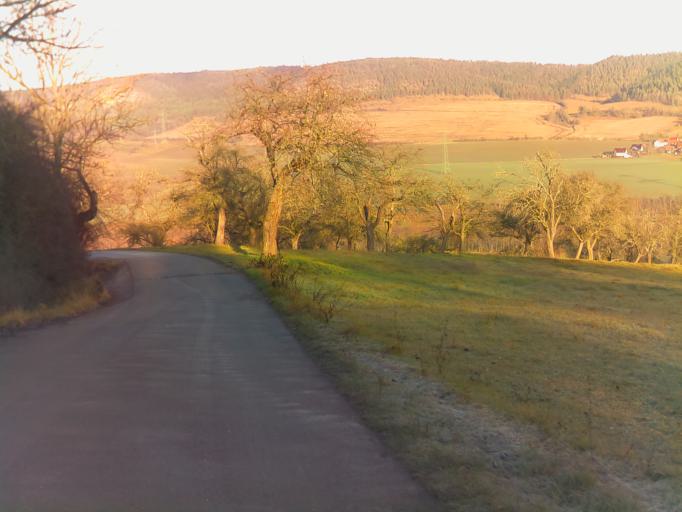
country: DE
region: Thuringia
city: Gumperda
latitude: 50.8024
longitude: 11.5132
